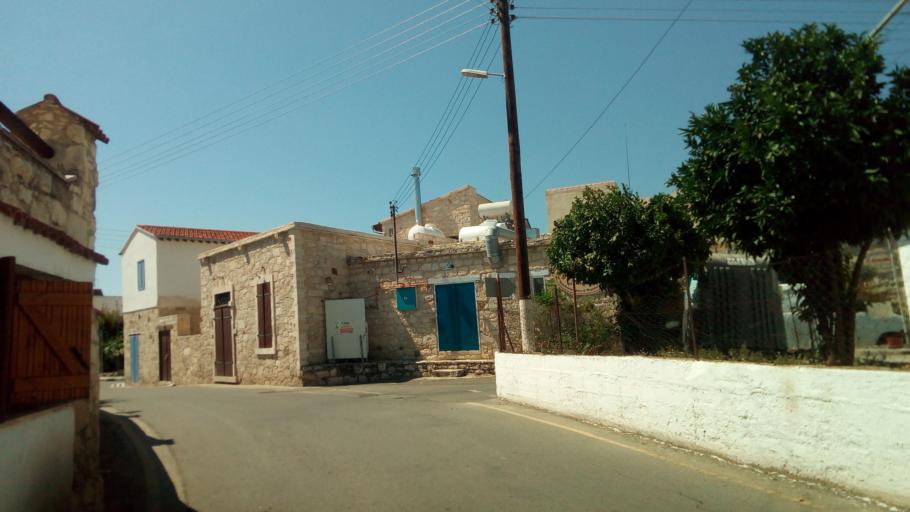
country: CY
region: Limassol
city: Parekklisha
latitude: 34.7439
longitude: 33.1598
